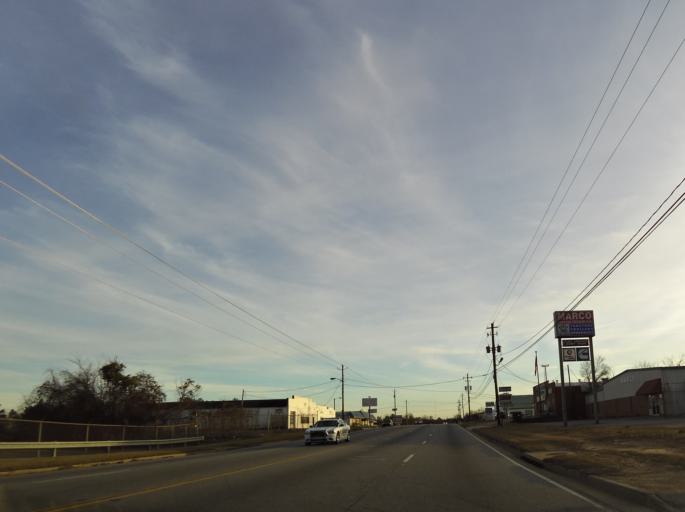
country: US
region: Georgia
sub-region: Bibb County
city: Macon
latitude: 32.8069
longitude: -83.6404
